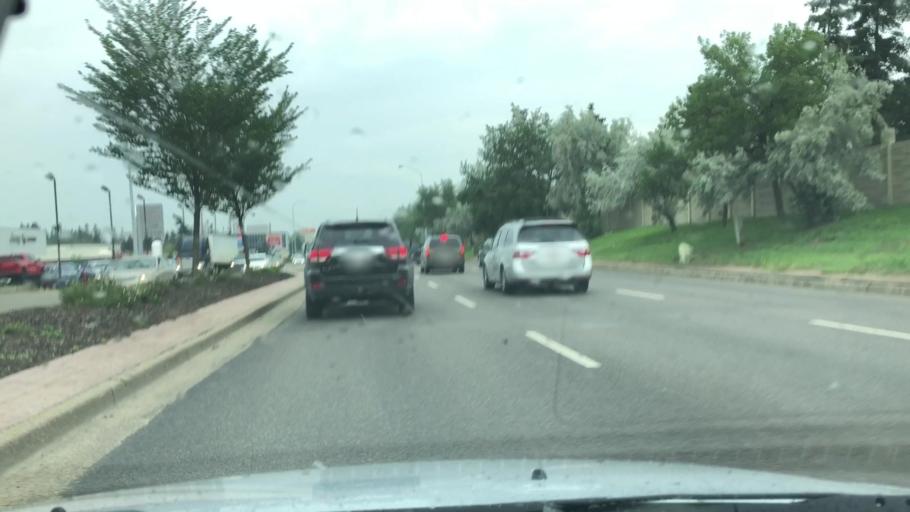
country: CA
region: Alberta
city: St. Albert
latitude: 53.6239
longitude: -113.6135
